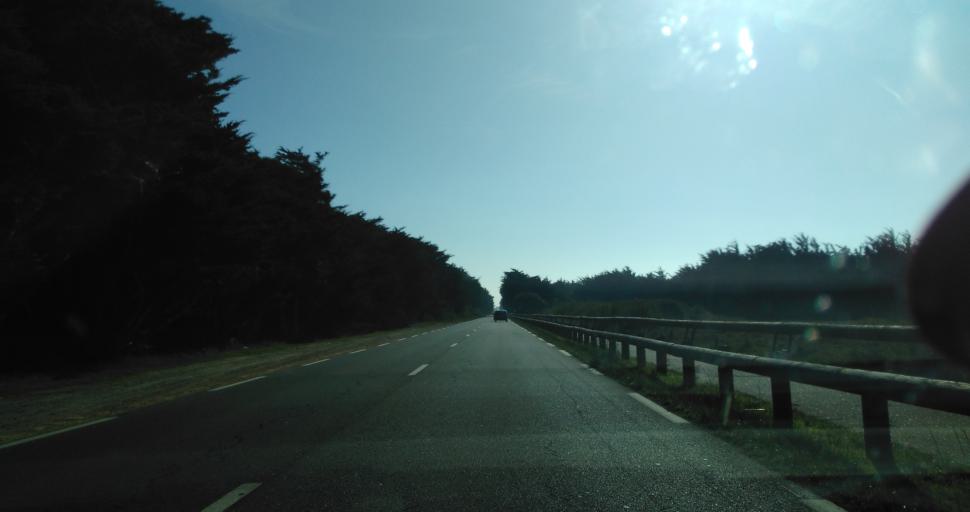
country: FR
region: Brittany
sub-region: Departement du Morbihan
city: Plouharnel
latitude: 47.5688
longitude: -3.1347
